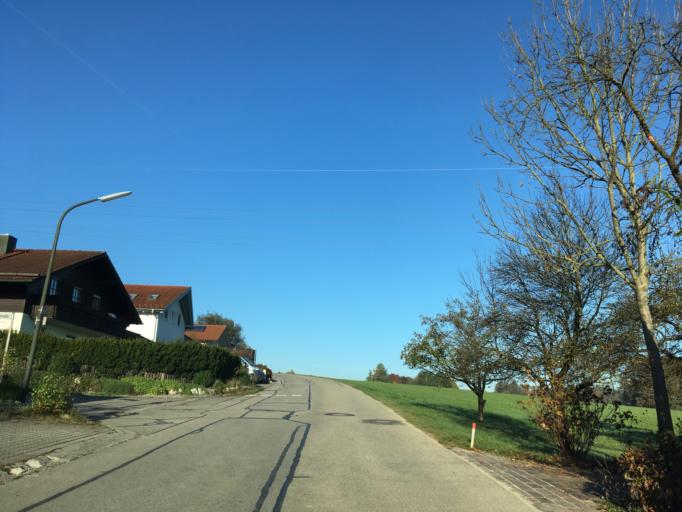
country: DE
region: Bavaria
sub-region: Upper Bavaria
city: Prutting
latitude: 47.8951
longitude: 12.1990
